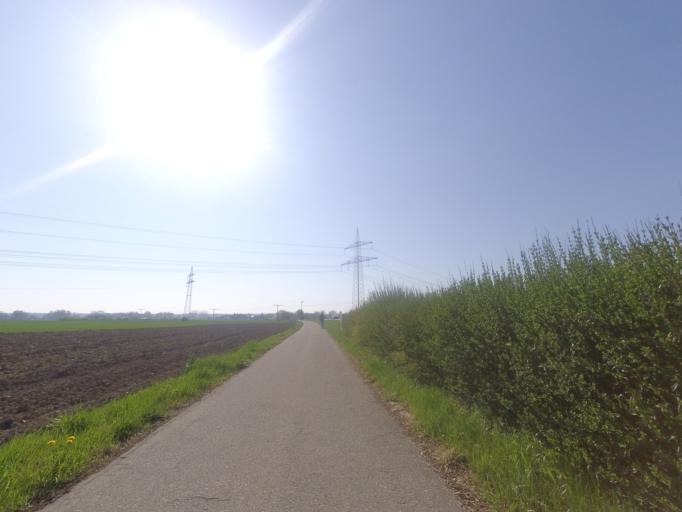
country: DE
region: Bavaria
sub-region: Swabia
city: Nersingen
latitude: 48.4225
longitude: 10.1292
